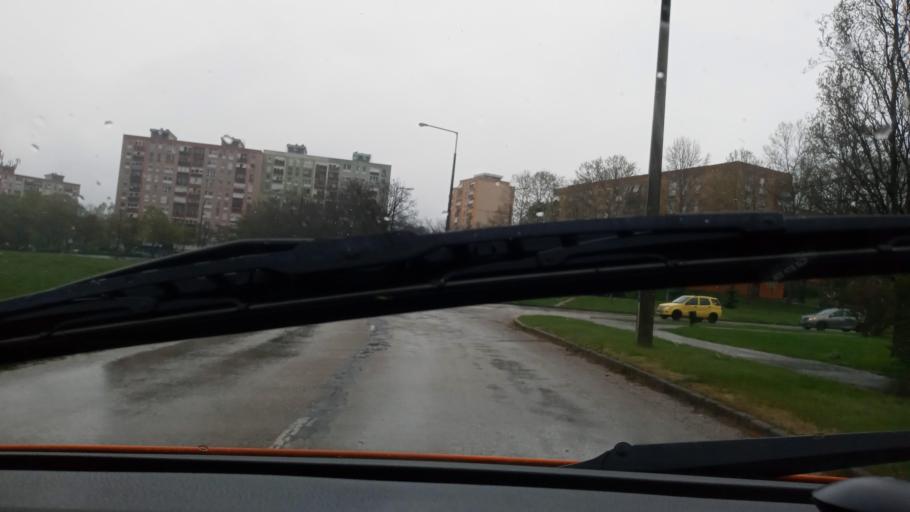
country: HU
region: Baranya
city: Pecs
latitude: 46.0372
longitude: 18.2187
